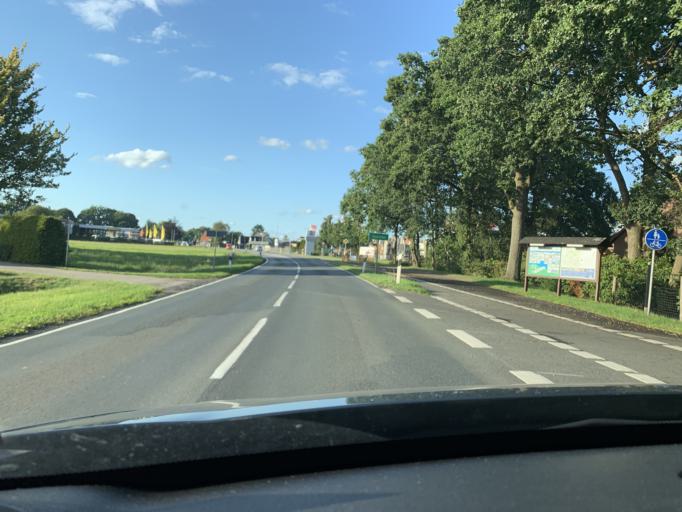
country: DE
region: Lower Saxony
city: Bad Zwischenahn
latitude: 53.1673
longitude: 8.0000
